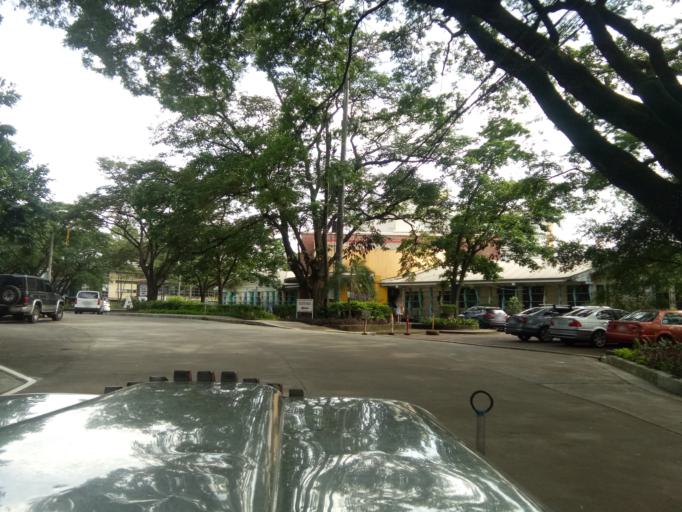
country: PH
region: Metro Manila
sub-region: Quezon City
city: Quezon City
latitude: 14.6524
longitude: 121.0651
